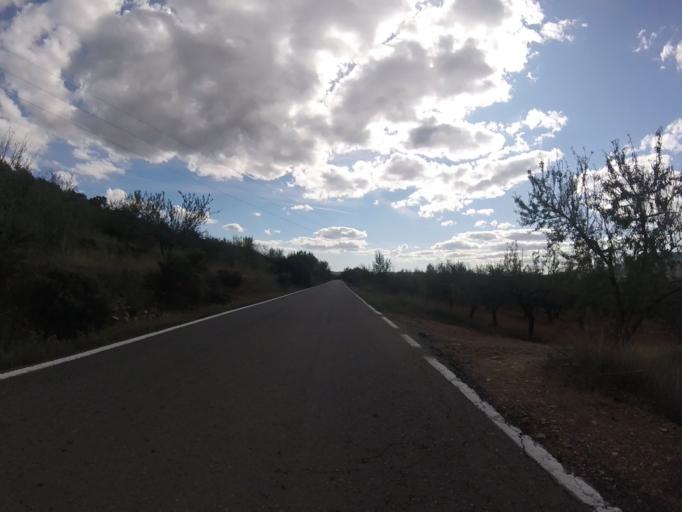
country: ES
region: Valencia
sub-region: Provincia de Castello
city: Cuevas de Vinroma
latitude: 40.3593
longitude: 0.1253
